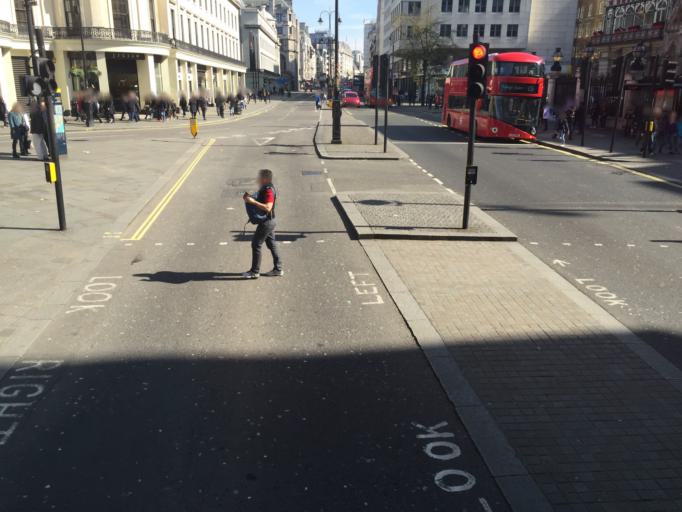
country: GB
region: England
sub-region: Greater London
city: London
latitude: 51.5083
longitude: -0.1259
